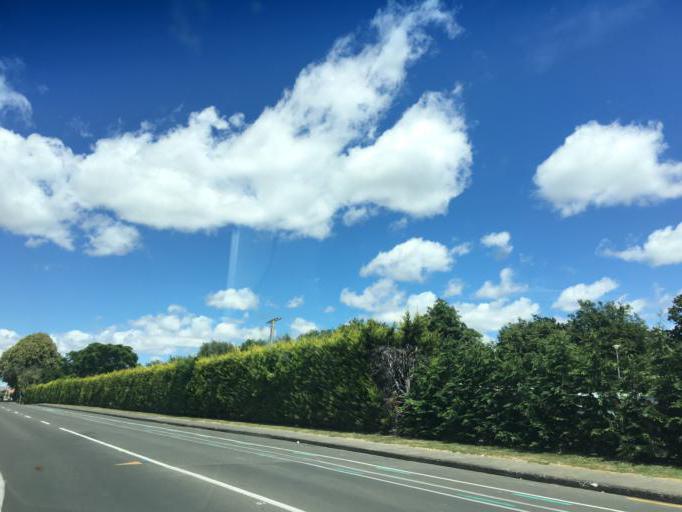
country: NZ
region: Hawke's Bay
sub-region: Hastings District
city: Hastings
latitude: -39.6482
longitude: 176.8630
